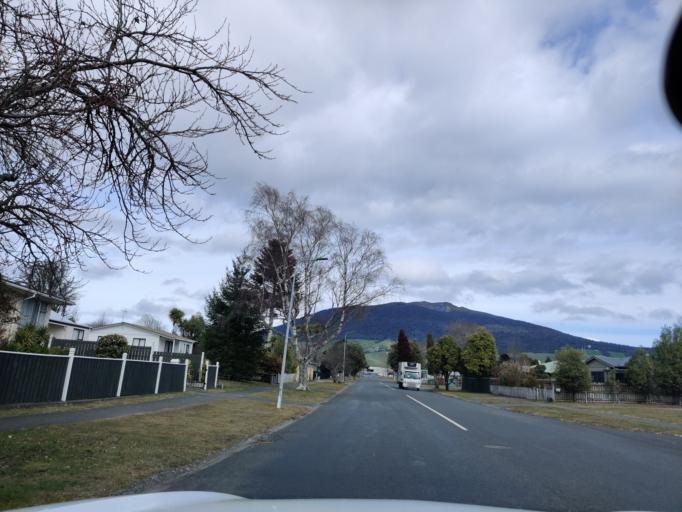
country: NZ
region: Waikato
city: Turangi
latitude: -38.9921
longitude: 175.8044
